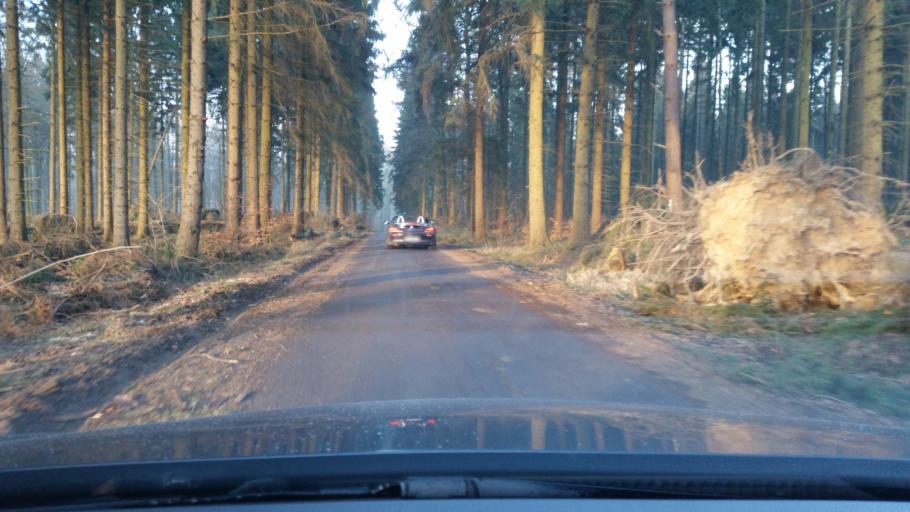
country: DE
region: Lower Saxony
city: Aerzen
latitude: 52.0860
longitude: 9.2977
